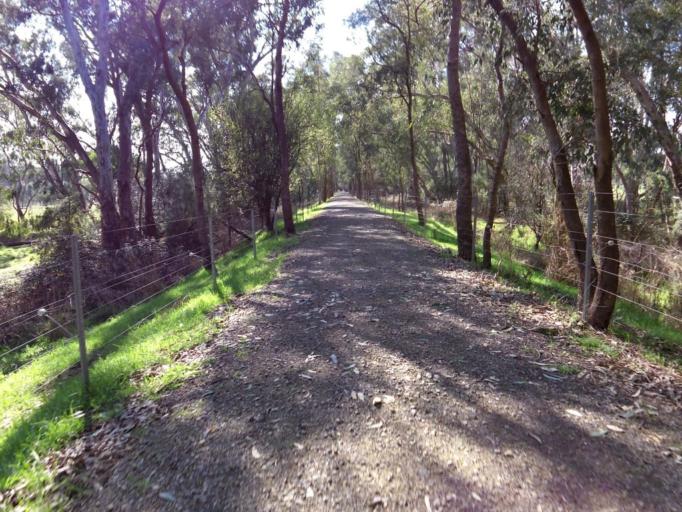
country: AU
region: Victoria
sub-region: Murrindindi
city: Alexandra
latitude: -37.1585
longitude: 145.5682
